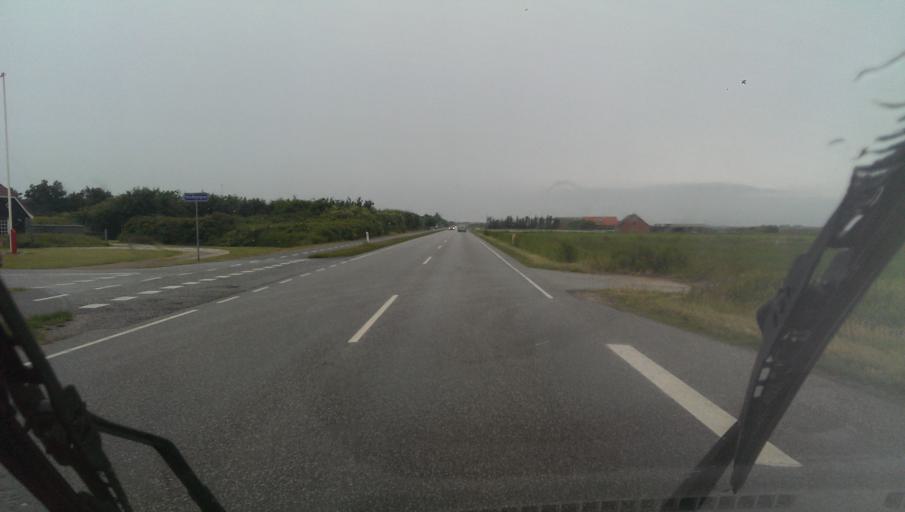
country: DK
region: Central Jutland
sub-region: Ringkobing-Skjern Kommune
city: Hvide Sande
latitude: 56.1095
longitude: 8.1234
